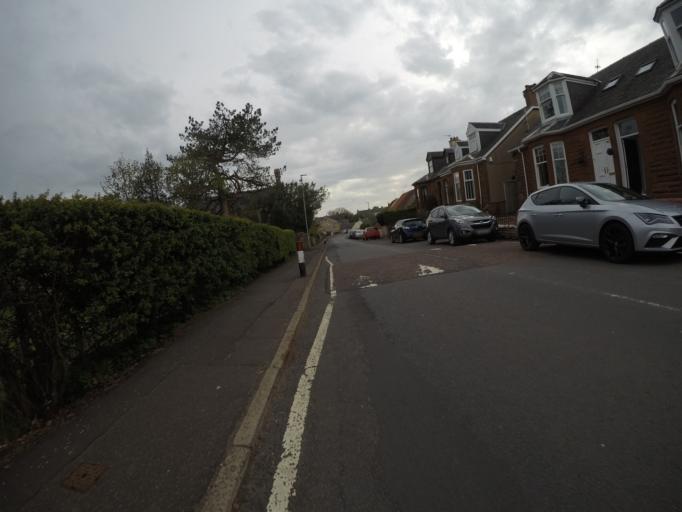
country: GB
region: Scotland
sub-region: East Ayrshire
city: Kilmaurs
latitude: 55.6391
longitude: -4.5231
